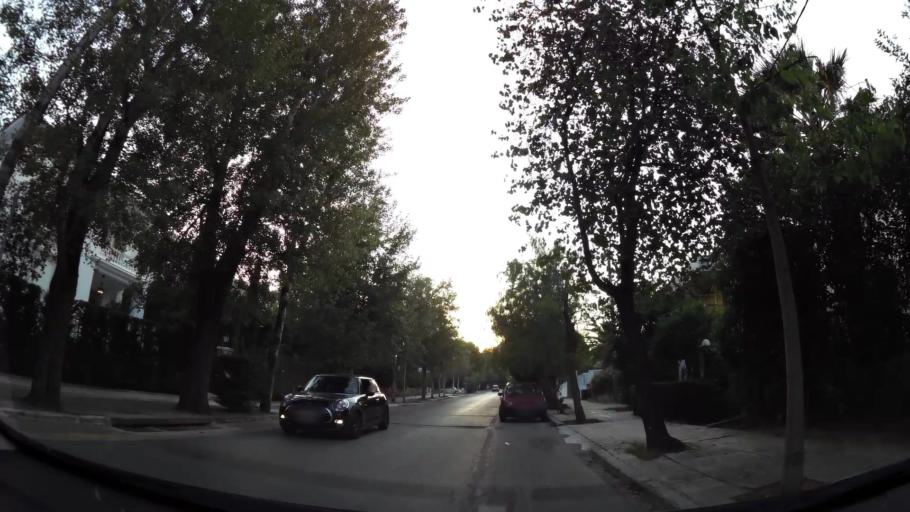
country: GR
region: Attica
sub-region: Nomarchia Athinas
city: Psychiko
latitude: 38.0105
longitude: 23.7731
